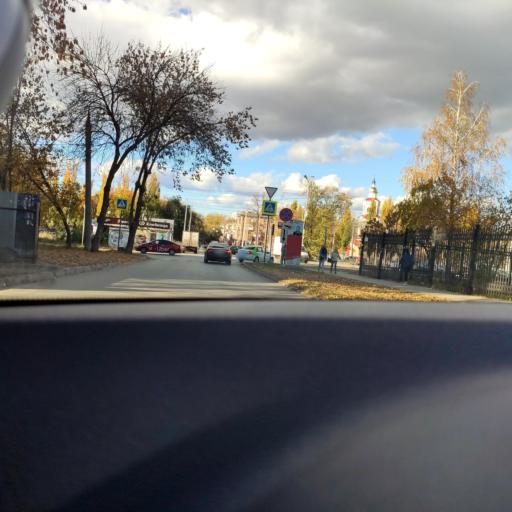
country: RU
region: Samara
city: Samara
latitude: 53.2035
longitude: 50.1650
